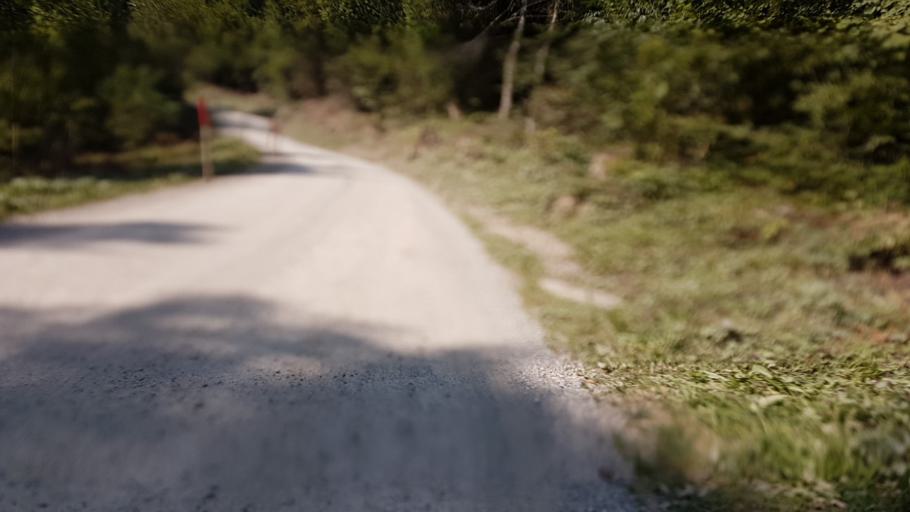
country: CH
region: Bern
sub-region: Frutigen-Niedersimmental District
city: Aeschi
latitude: 46.6321
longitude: 7.7422
